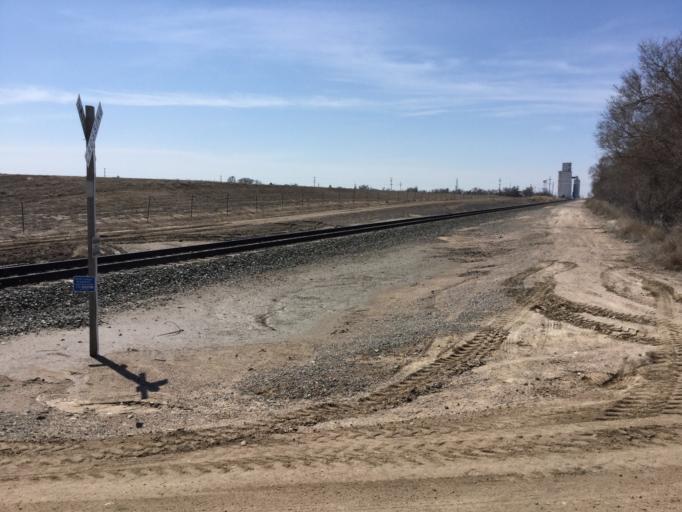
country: US
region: Kansas
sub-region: Kearny County
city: Lakin
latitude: 37.9441
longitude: -101.2449
